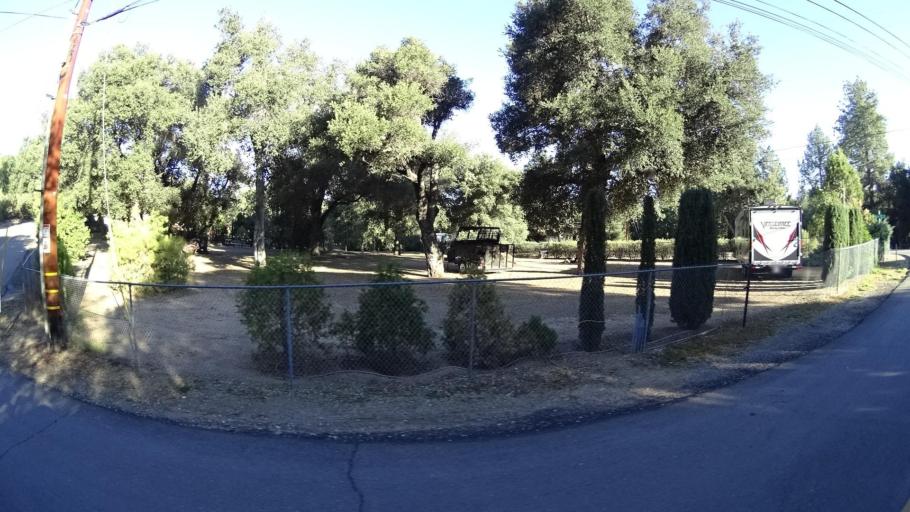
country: US
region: California
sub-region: San Diego County
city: Pine Valley
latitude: 32.8187
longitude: -116.5255
